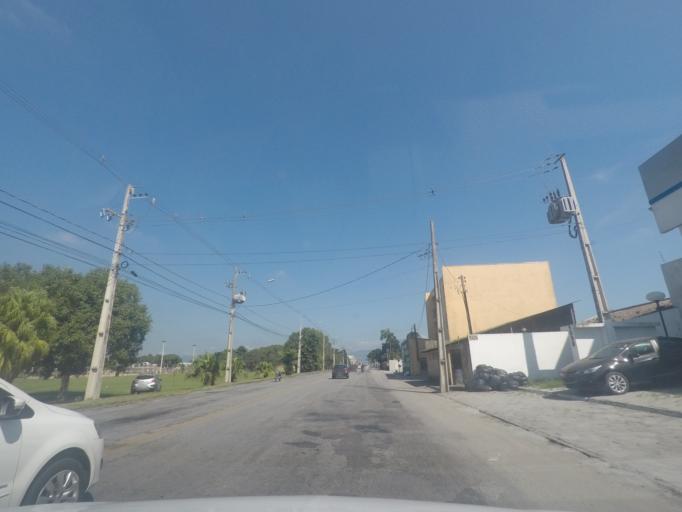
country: BR
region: Parana
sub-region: Paranagua
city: Paranagua
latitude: -25.5421
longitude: -48.5368
